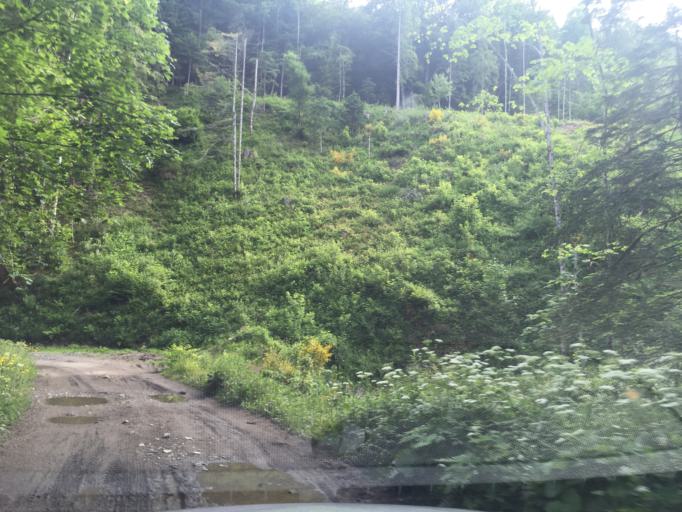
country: FR
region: Rhone-Alpes
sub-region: Departement de la Savoie
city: La Rochette
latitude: 45.4365
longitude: 6.1631
